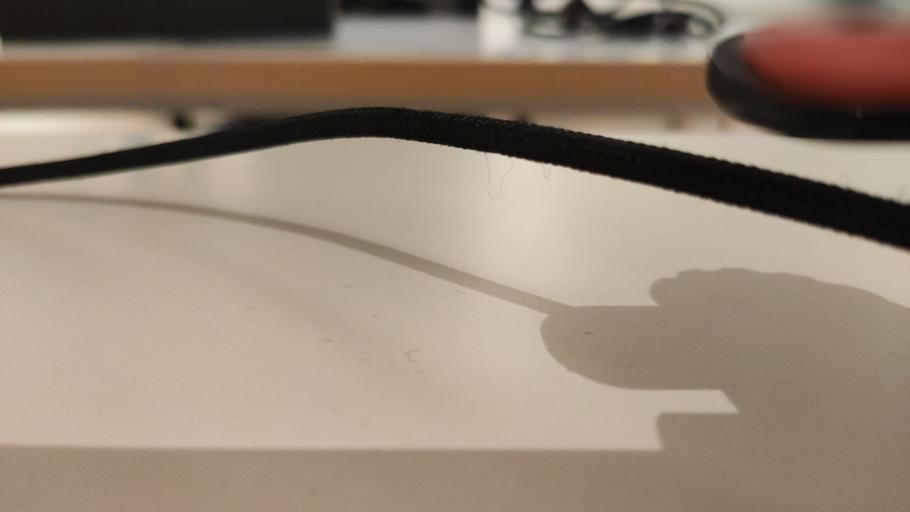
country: RU
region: Moskovskaya
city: Dorokhovo
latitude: 55.3856
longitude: 36.3966
